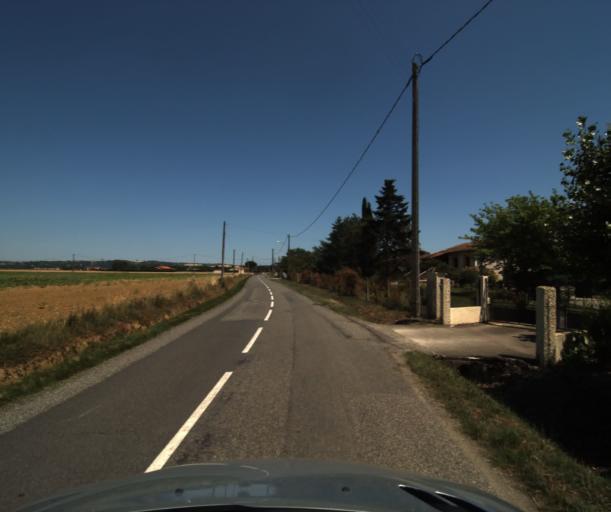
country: FR
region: Midi-Pyrenees
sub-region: Departement de la Haute-Garonne
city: Saubens
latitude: 43.4774
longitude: 1.3630
